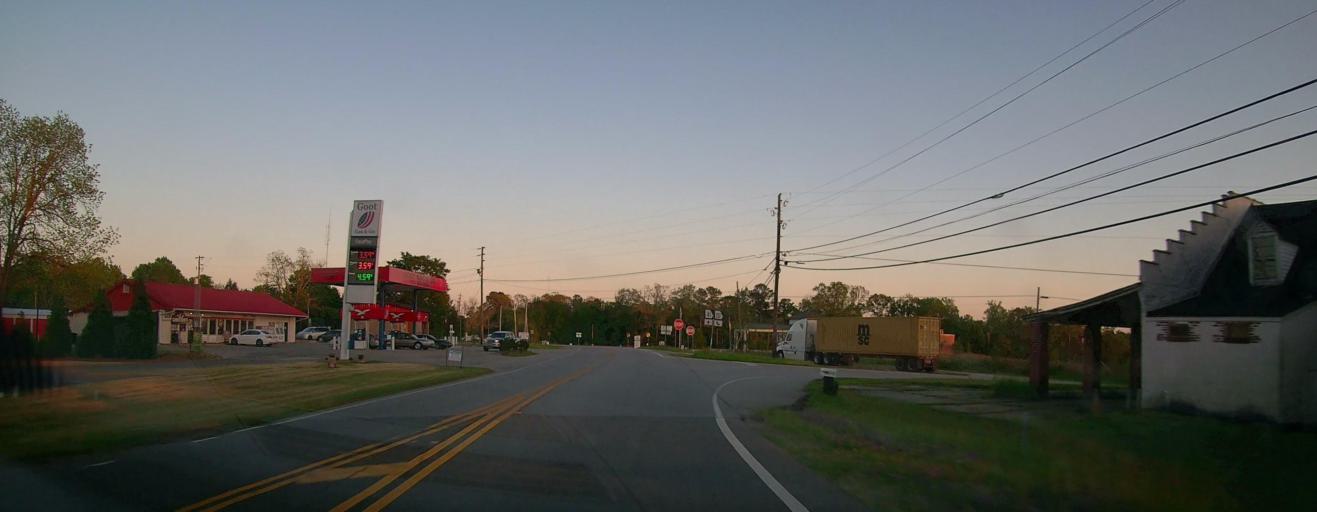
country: US
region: Georgia
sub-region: Marion County
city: Buena Vista
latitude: 32.3332
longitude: -84.5295
